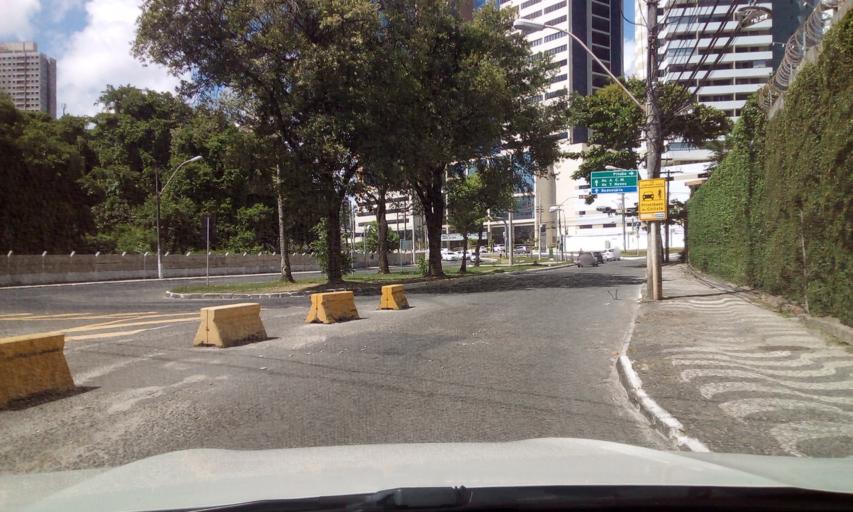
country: BR
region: Bahia
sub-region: Salvador
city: Salvador
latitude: -12.9900
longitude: -38.4666
